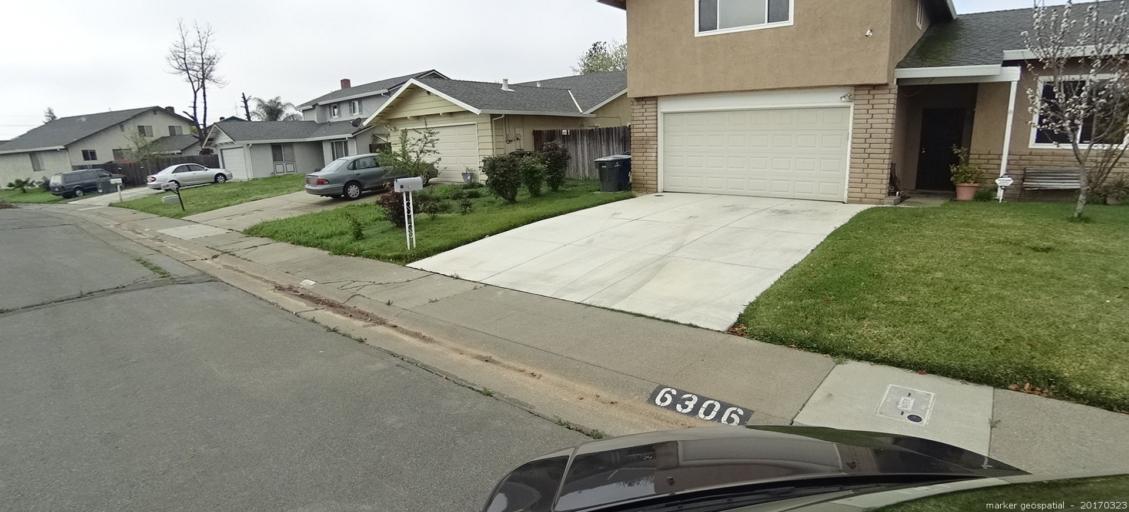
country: US
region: California
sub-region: Sacramento County
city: Florin
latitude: 38.5121
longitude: -121.4215
